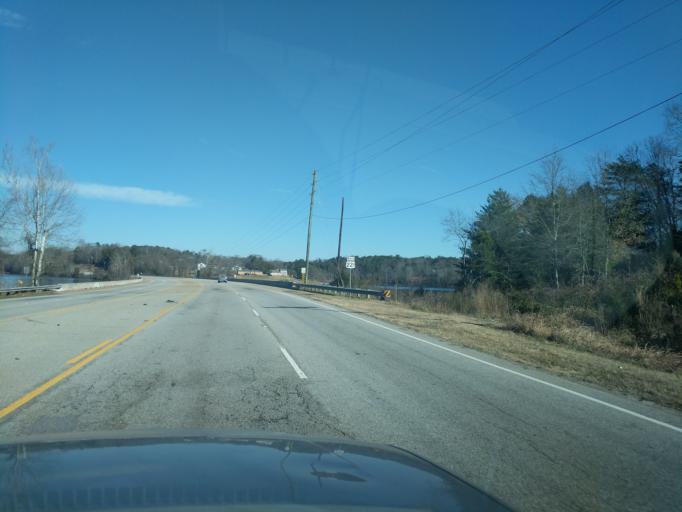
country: US
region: South Carolina
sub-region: Spartanburg County
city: Mayo
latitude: 35.0641
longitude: -81.8792
